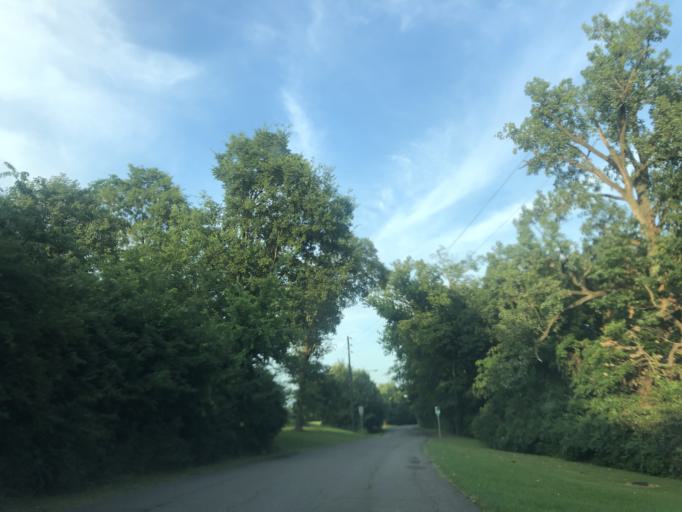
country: US
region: Tennessee
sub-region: Davidson County
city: Nashville
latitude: 36.1642
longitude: -86.7399
